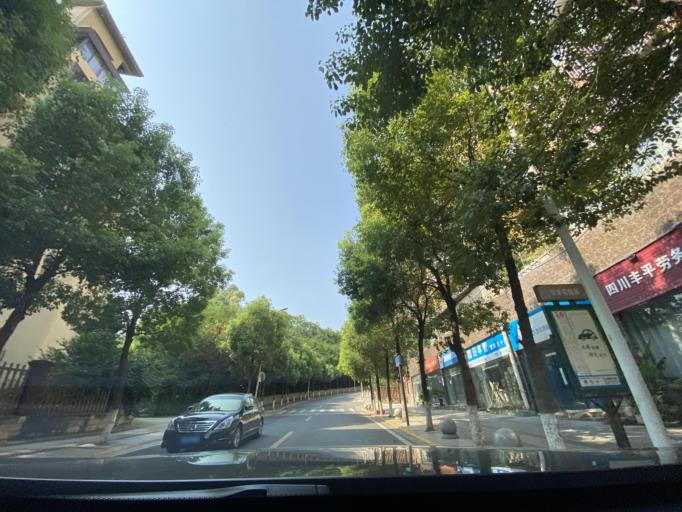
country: CN
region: Sichuan
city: Jiancheng
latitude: 30.4182
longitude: 104.5441
